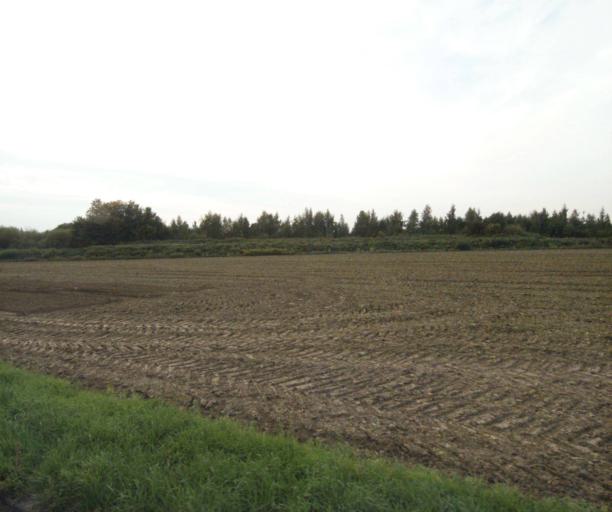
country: FR
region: Nord-Pas-de-Calais
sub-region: Departement du Nord
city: Seclin
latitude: 50.5425
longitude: 3.0348
